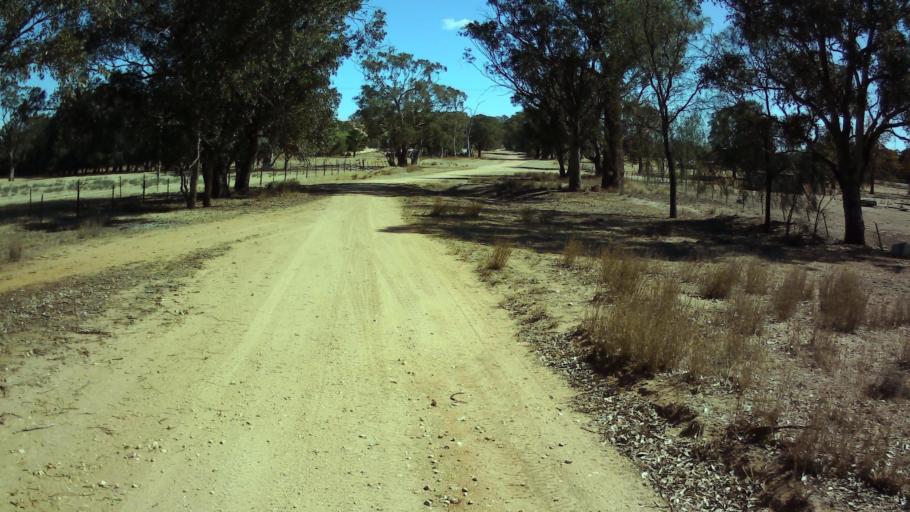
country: AU
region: New South Wales
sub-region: Weddin
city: Grenfell
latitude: -34.0070
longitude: 148.4354
